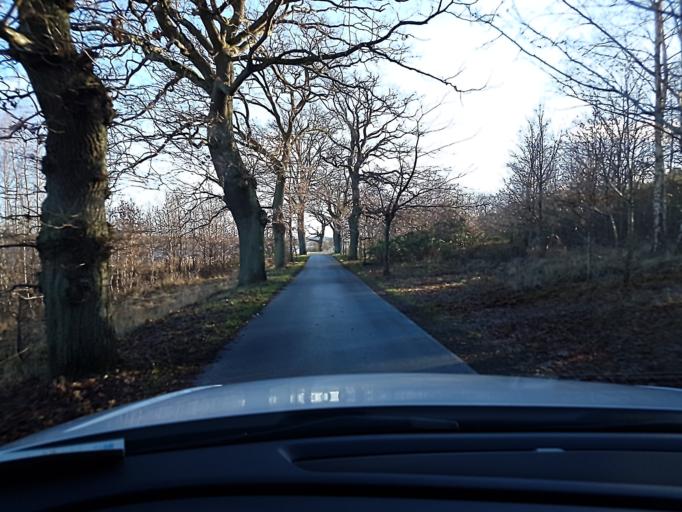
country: DE
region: Mecklenburg-Vorpommern
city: Ostseebad Sellin
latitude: 54.3651
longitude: 13.6796
